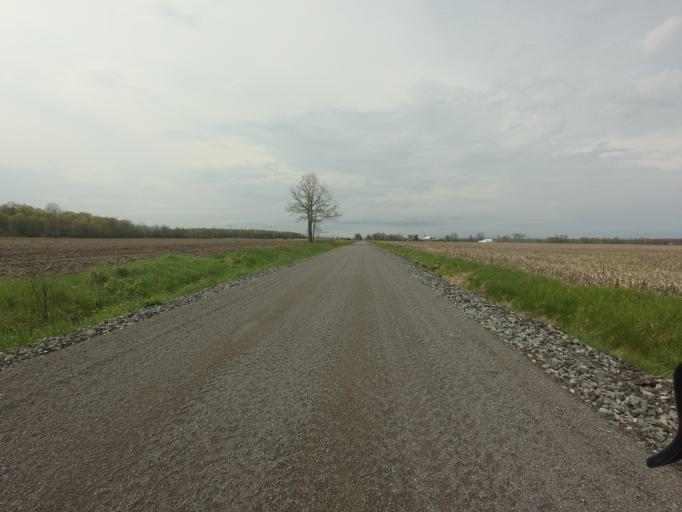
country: CA
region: Ontario
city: Carleton Place
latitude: 45.1736
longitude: -76.1528
